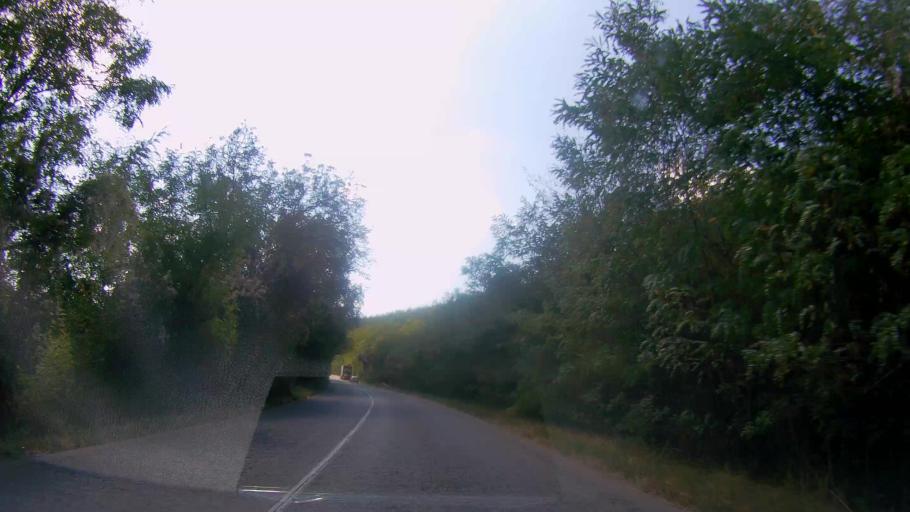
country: BG
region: Veliko Turnovo
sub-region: Obshtina Polski Trumbesh
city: Polski Trumbesh
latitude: 43.4393
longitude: 25.6542
